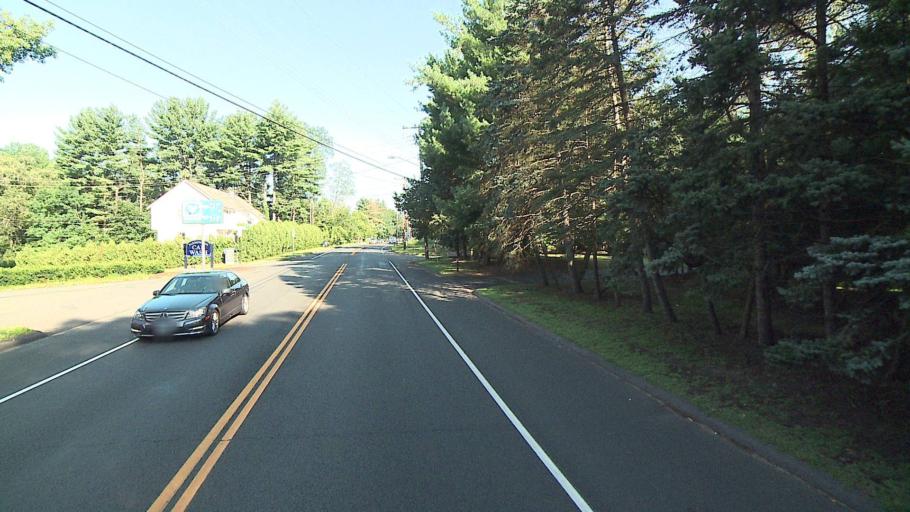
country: US
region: Connecticut
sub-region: Hartford County
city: Farmington
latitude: 41.7435
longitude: -72.8598
